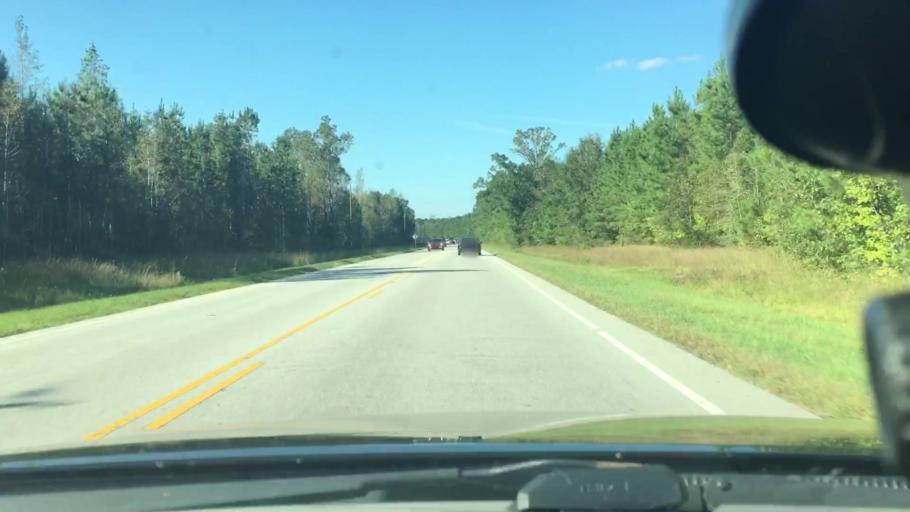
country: US
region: North Carolina
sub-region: Craven County
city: Vanceboro
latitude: 35.2959
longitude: -77.1307
